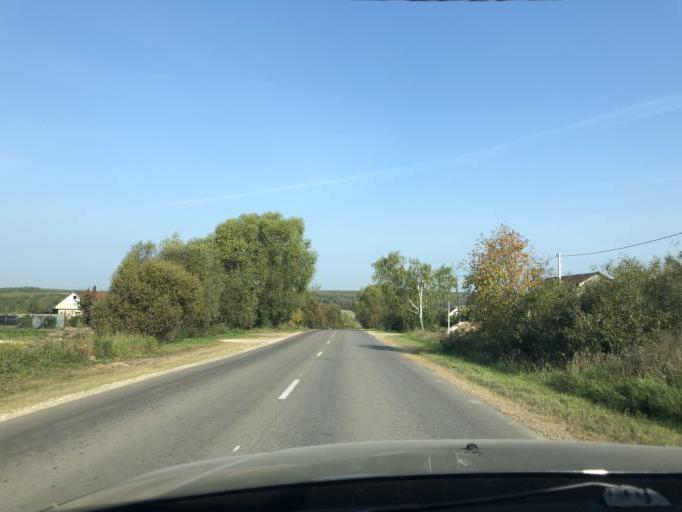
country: RU
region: Tula
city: Novogurovskiy
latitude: 54.3508
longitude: 37.3553
